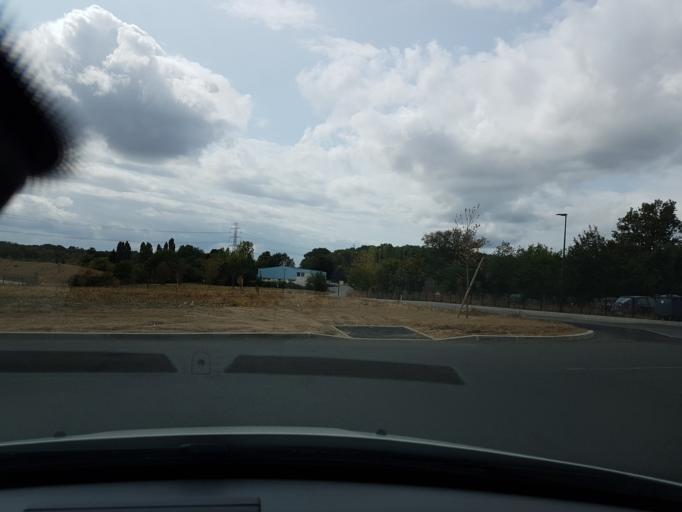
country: FR
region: Centre
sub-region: Departement d'Indre-et-Loire
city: Chambray-les-Tours
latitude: 47.3270
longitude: 0.7031
